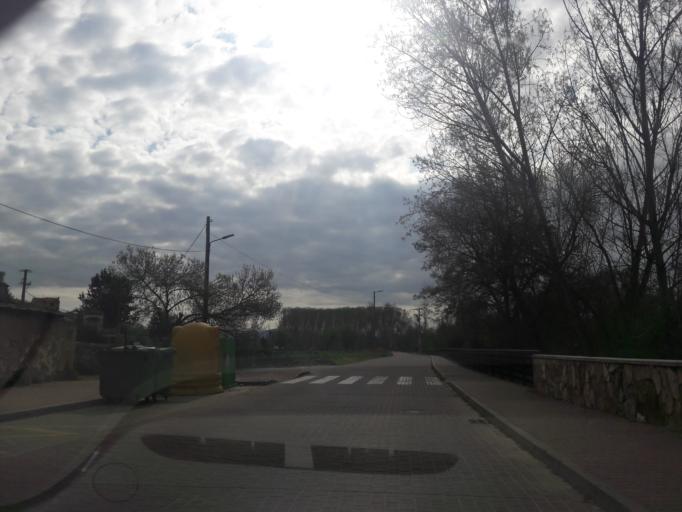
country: ES
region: Castille and Leon
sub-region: Provincia de Salamanca
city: Ciudad Rodrigo
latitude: 40.5945
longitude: -6.5329
